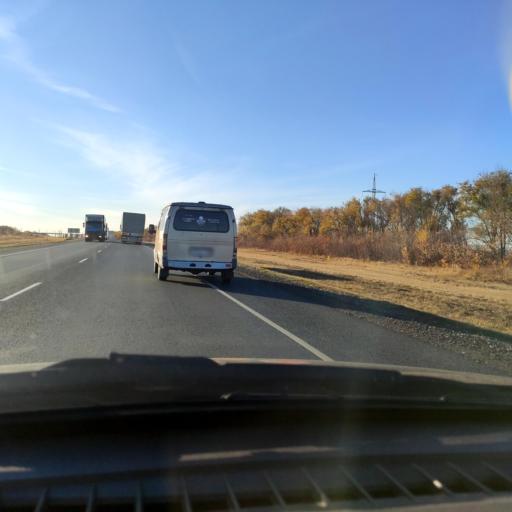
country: RU
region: Samara
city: Varlamovo
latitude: 53.1965
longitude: 48.3101
